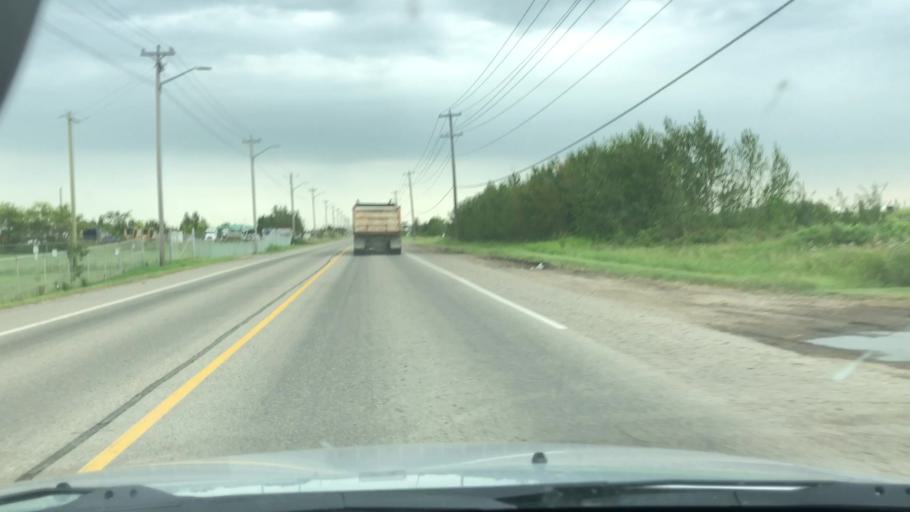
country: CA
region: Alberta
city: Sherwood Park
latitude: 53.5249
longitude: -113.3939
